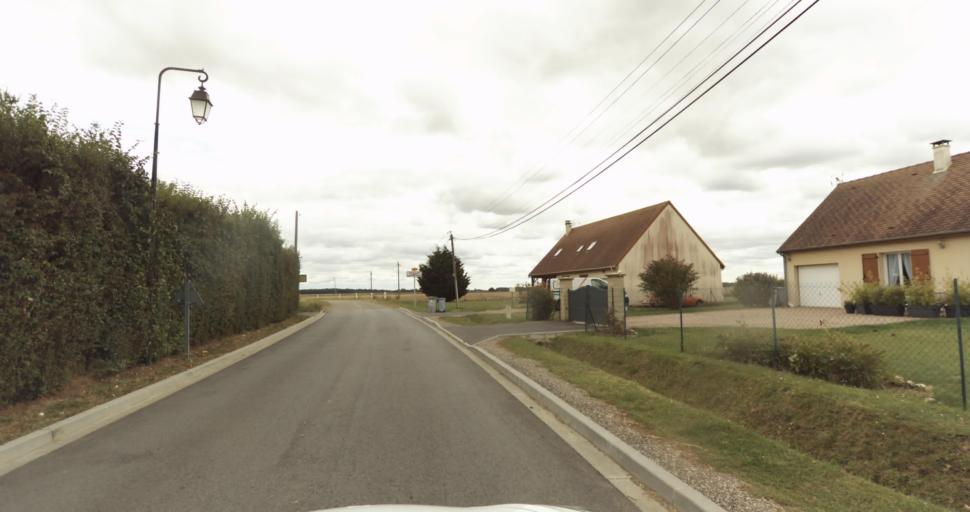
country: FR
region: Haute-Normandie
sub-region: Departement de l'Eure
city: La Madeleine-de-Nonancourt
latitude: 48.8331
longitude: 1.2030
